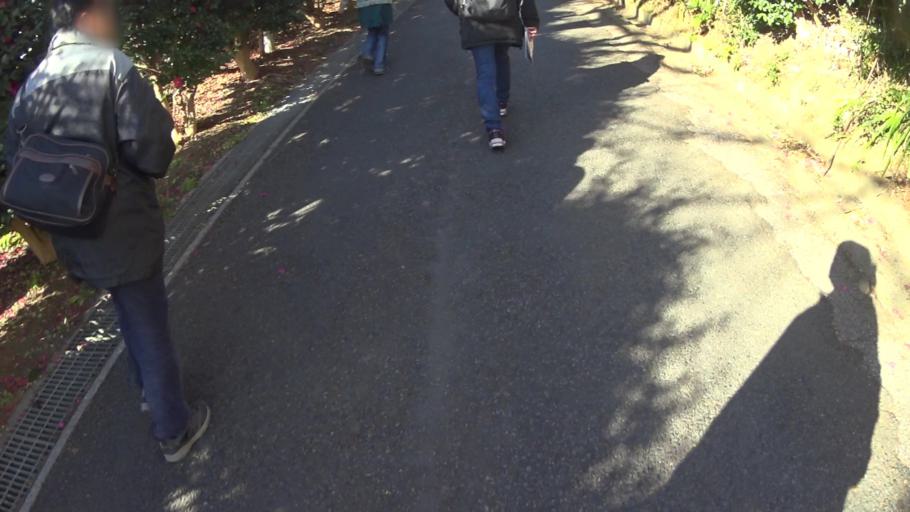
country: JP
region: Saitama
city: Shimotoda
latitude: 35.8415
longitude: 139.6882
